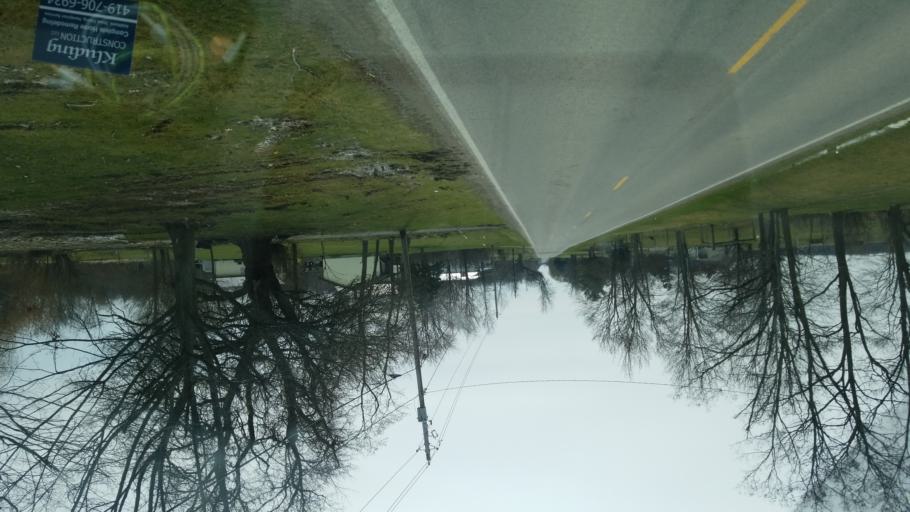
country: US
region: Ohio
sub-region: Huron County
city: Wakeman
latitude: 41.2330
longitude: -82.4915
